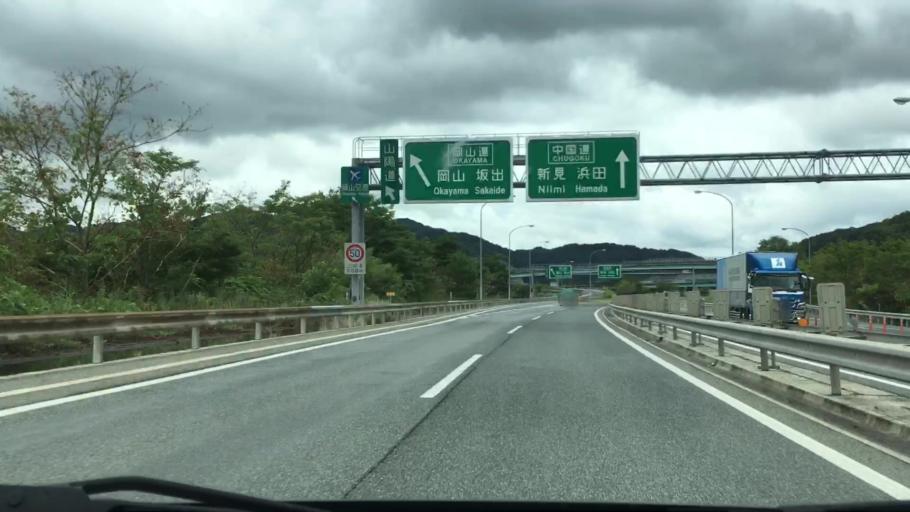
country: JP
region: Okayama
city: Takahashi
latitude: 34.9862
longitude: 133.6867
